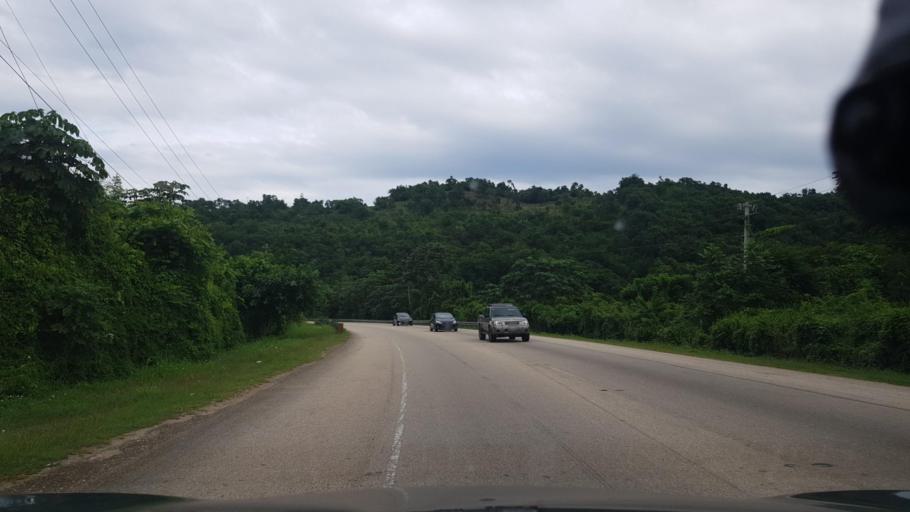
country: JM
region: Saint Ann
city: Discovery Bay
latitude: 18.4623
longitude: -77.4524
